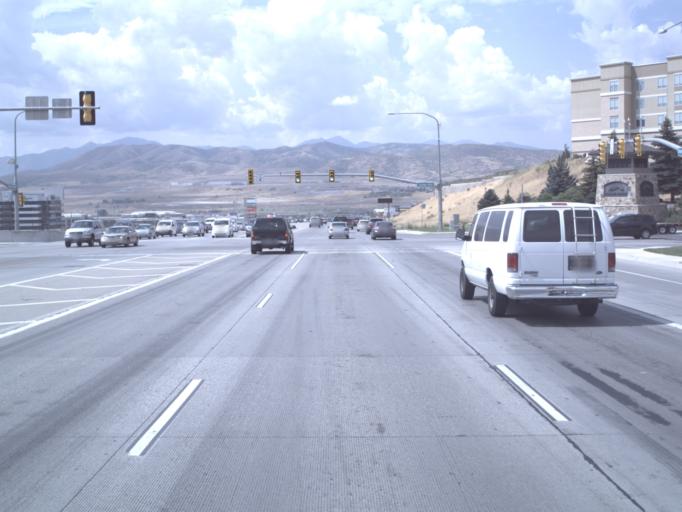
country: US
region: Utah
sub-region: Utah County
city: Lehi
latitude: 40.4318
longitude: -111.8801
